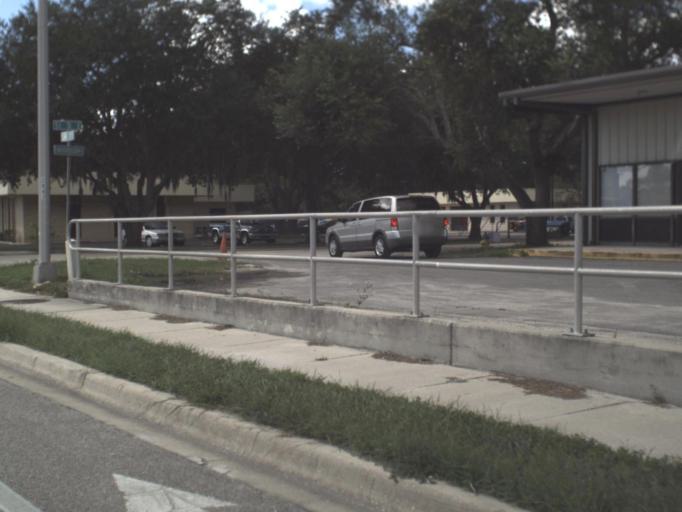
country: US
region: Florida
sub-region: Manatee County
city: Samoset
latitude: 27.4464
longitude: -82.4970
